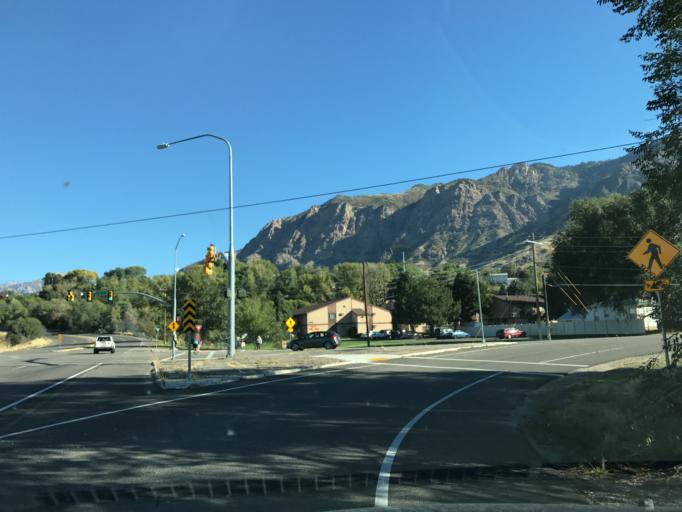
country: US
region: Utah
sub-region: Weber County
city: Ogden
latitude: 41.2414
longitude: -111.9453
